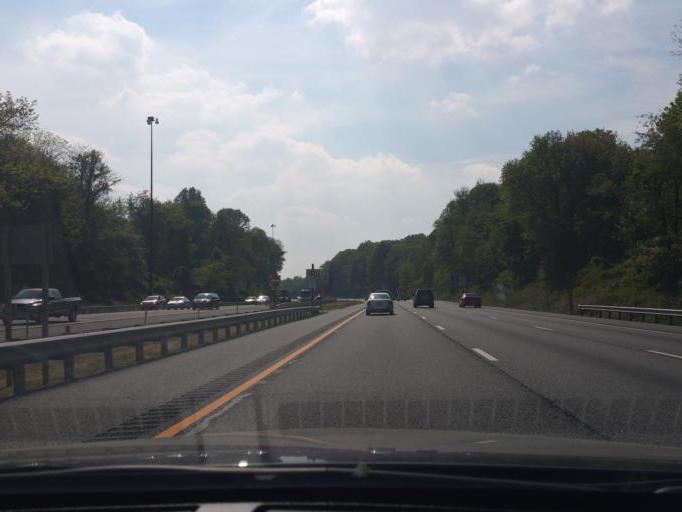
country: US
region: Maryland
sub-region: Harford County
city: Havre de Grace
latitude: 39.5766
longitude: -76.1232
